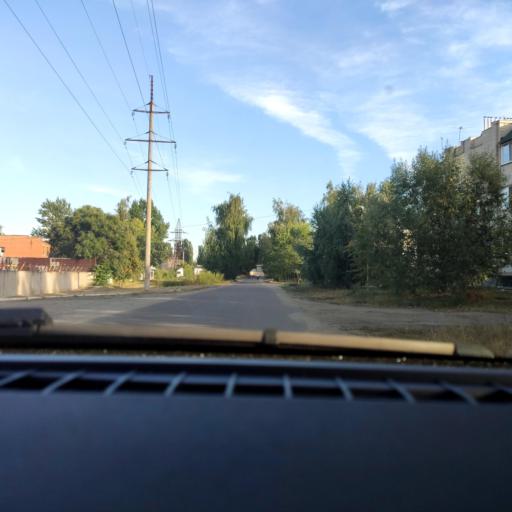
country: RU
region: Voronezj
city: Maslovka
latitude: 51.5797
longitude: 39.2977
